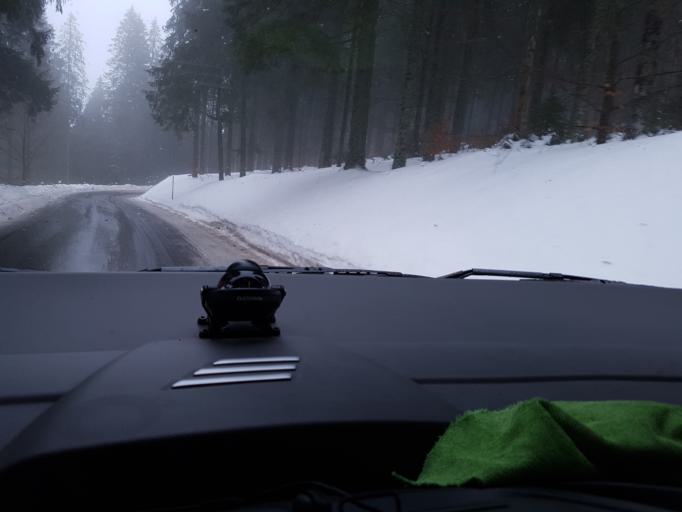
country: FR
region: Lorraine
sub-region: Departement des Vosges
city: Plainfaing
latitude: 48.1358
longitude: 7.0646
